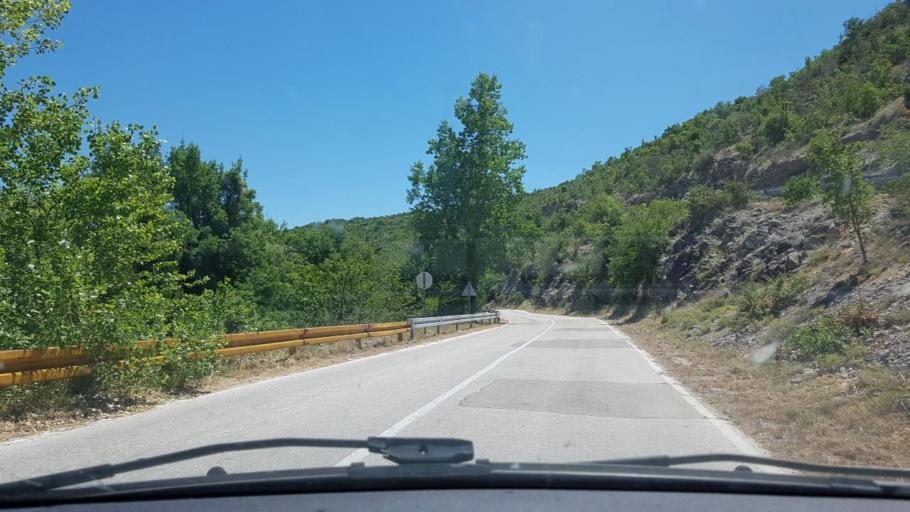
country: HR
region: Sibensko-Kniniska
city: Kistanje
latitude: 44.0108
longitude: 16.0348
